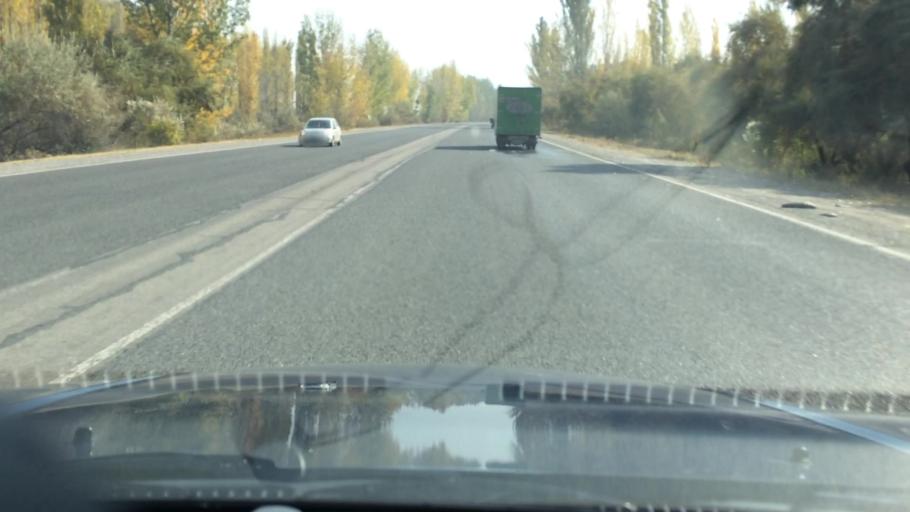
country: KG
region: Chuy
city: Ivanovka
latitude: 42.9374
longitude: 74.9870
